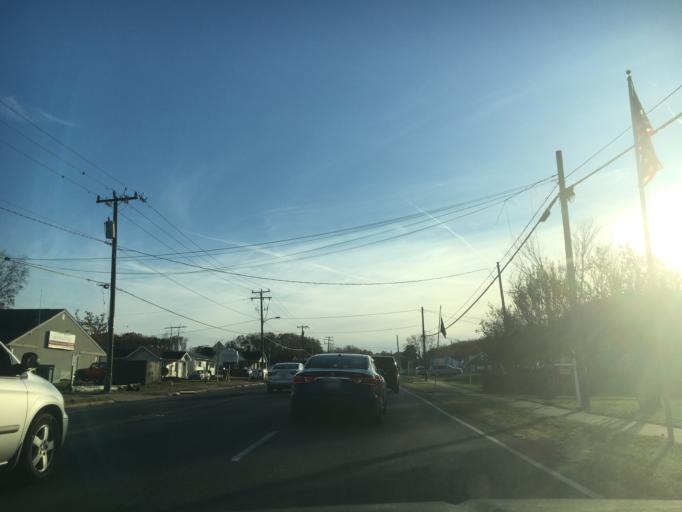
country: US
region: Virginia
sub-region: Prince William County
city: Dumfries
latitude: 38.5647
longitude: -77.3297
